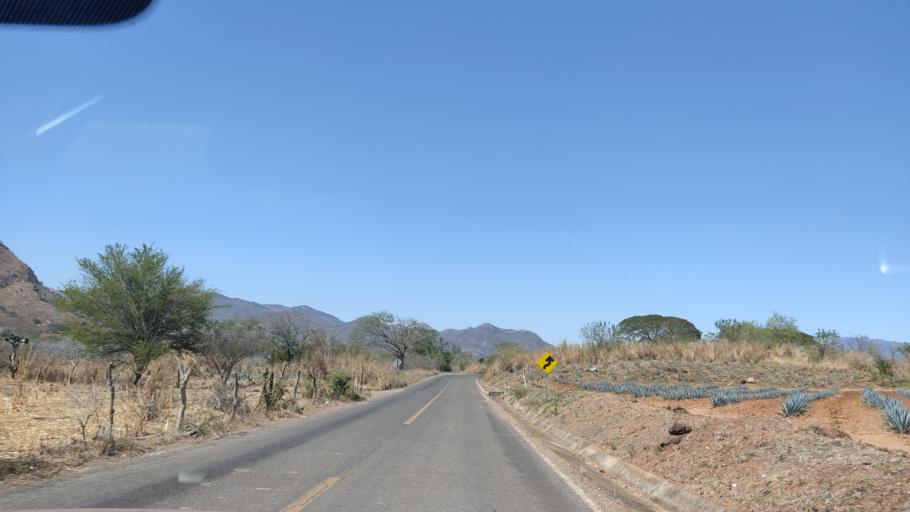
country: MX
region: Nayarit
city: Santa Maria del Oro
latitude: 21.4945
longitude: -104.6227
